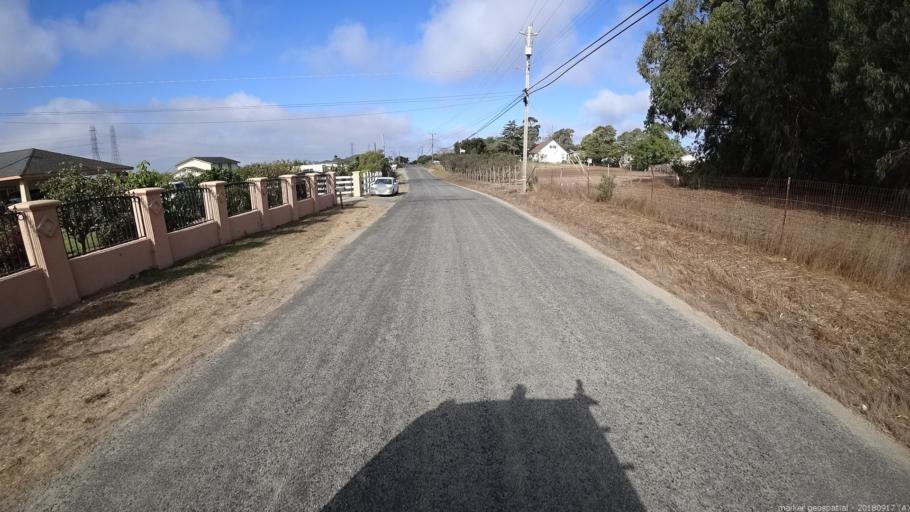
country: US
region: California
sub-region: Monterey County
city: Prunedale
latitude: 36.7914
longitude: -121.7045
